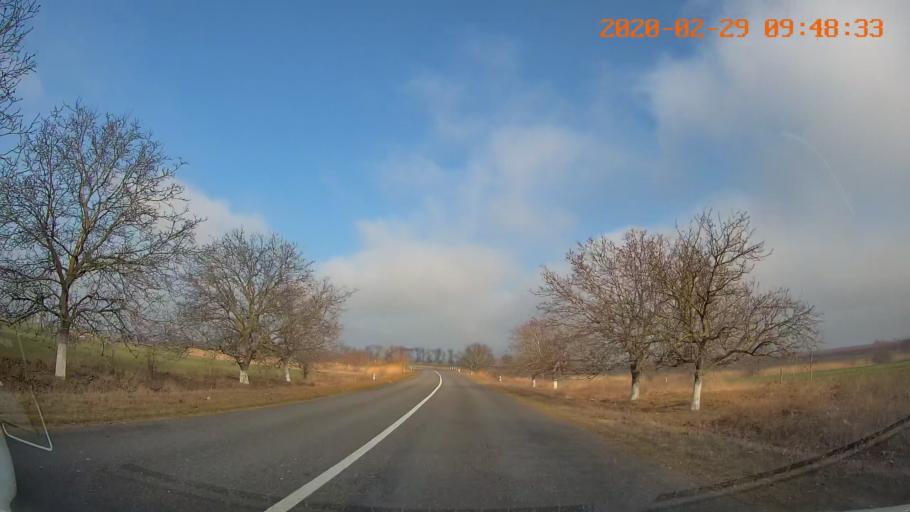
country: MD
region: Telenesti
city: Crasnoe
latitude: 46.6893
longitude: 29.7843
